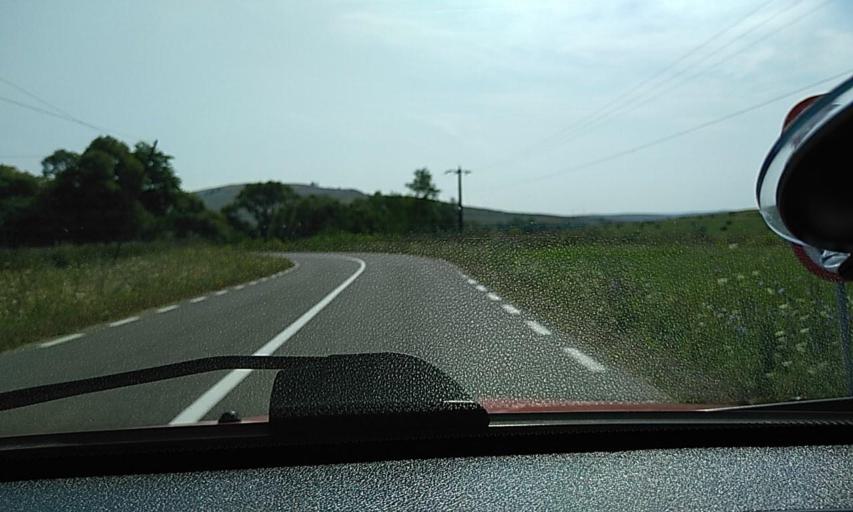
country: RO
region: Brasov
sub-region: Oras Rupea
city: Fiser
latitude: 46.0395
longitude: 25.1251
